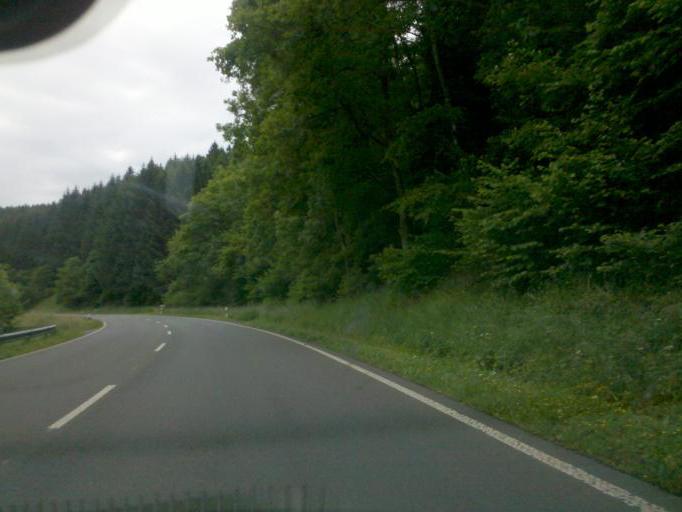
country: DE
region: North Rhine-Westphalia
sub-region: Regierungsbezirk Arnsberg
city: Olpe
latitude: 51.0291
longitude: 7.8931
